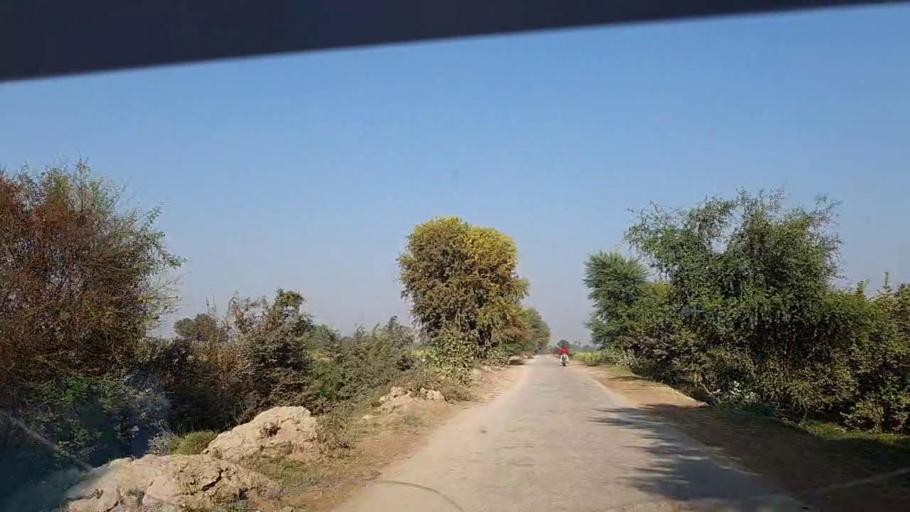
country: PK
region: Sindh
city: Sobhadero
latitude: 27.2473
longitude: 68.3260
